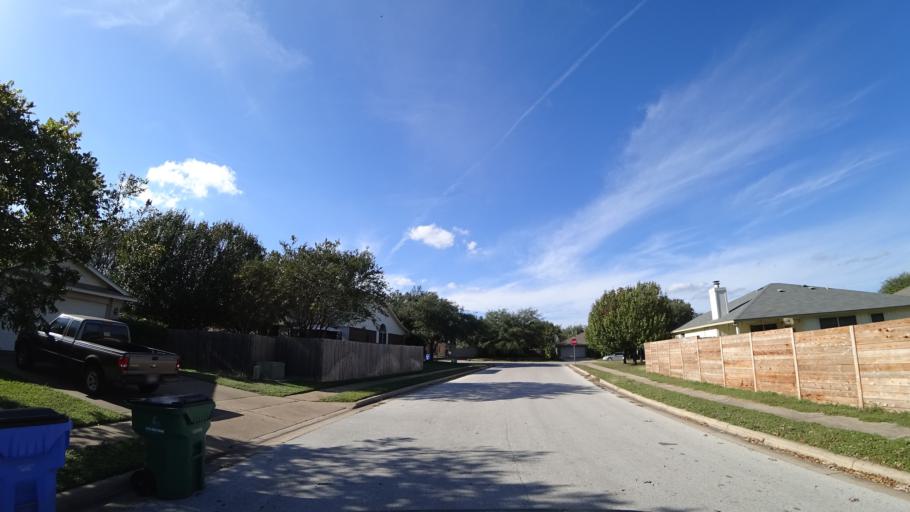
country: US
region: Texas
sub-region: Travis County
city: Wells Branch
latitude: 30.4627
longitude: -97.6851
